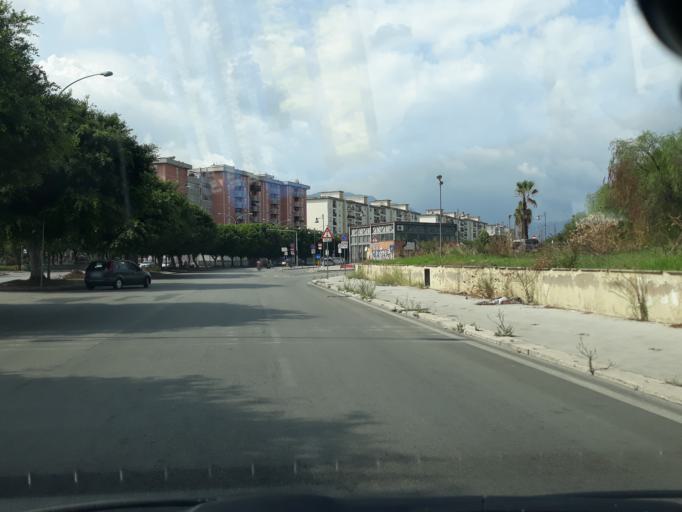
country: IT
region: Sicily
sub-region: Palermo
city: Palermo
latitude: 38.0989
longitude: 13.3464
